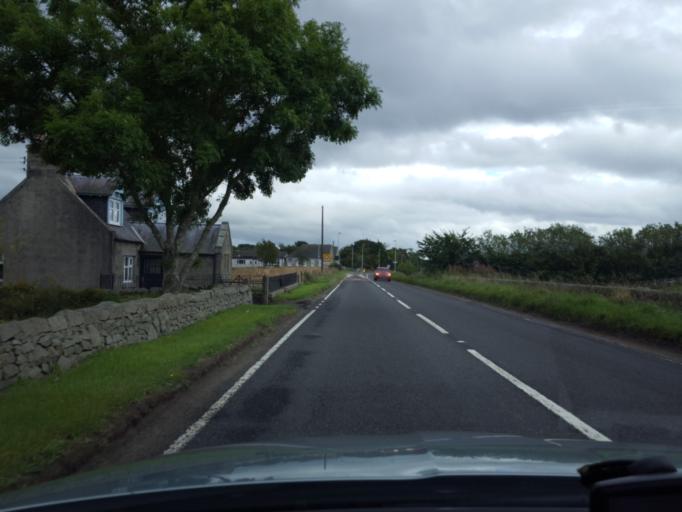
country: GB
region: Scotland
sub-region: Aberdeenshire
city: Kemnay
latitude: 57.1740
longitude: -2.4219
